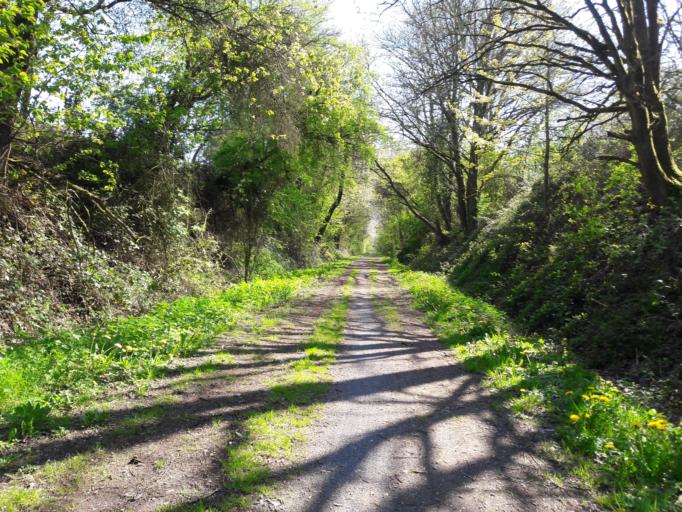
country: FR
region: Nord-Pas-de-Calais
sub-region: Departement du Nord
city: Sains-du-Nord
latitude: 50.1525
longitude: 4.0694
